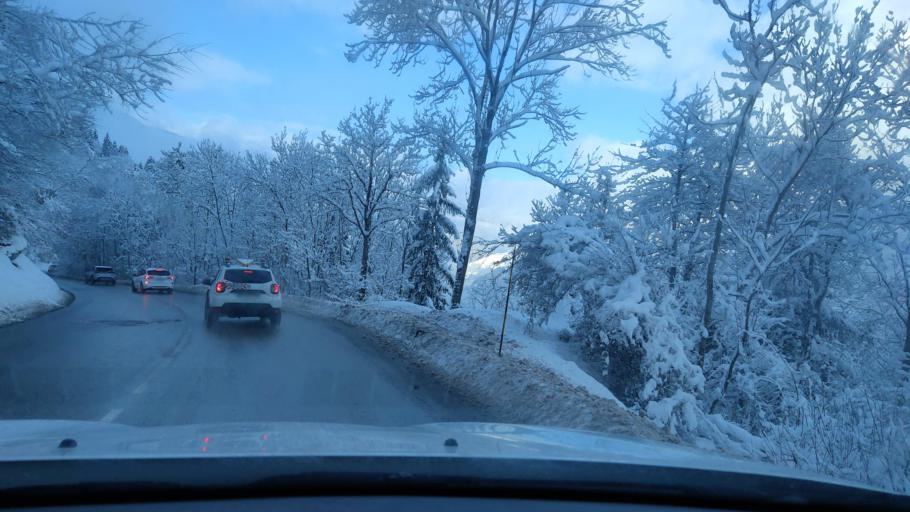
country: FR
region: Rhone-Alpes
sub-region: Departement de la Savoie
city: Saint-Bon-Tarentaise
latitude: 45.4415
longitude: 6.6191
